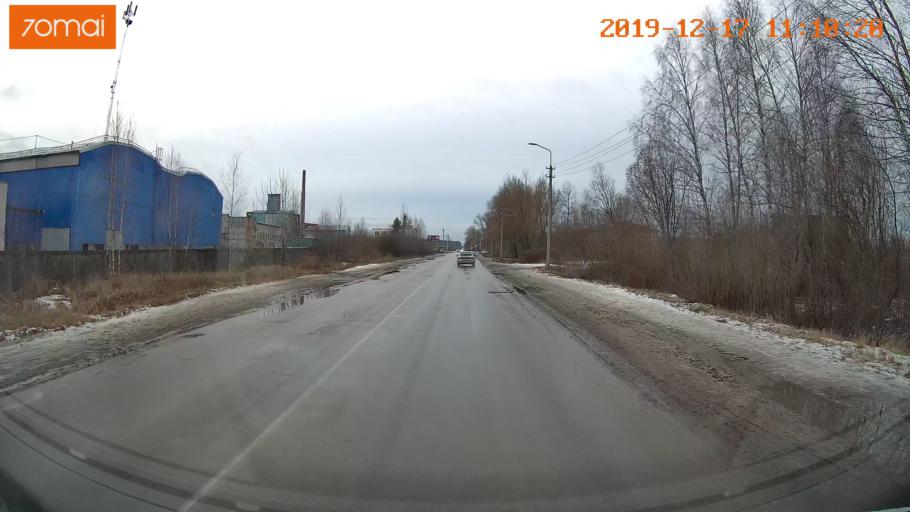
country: RU
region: Vladimir
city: Gus'-Khrustal'nyy
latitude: 55.5935
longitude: 40.6421
